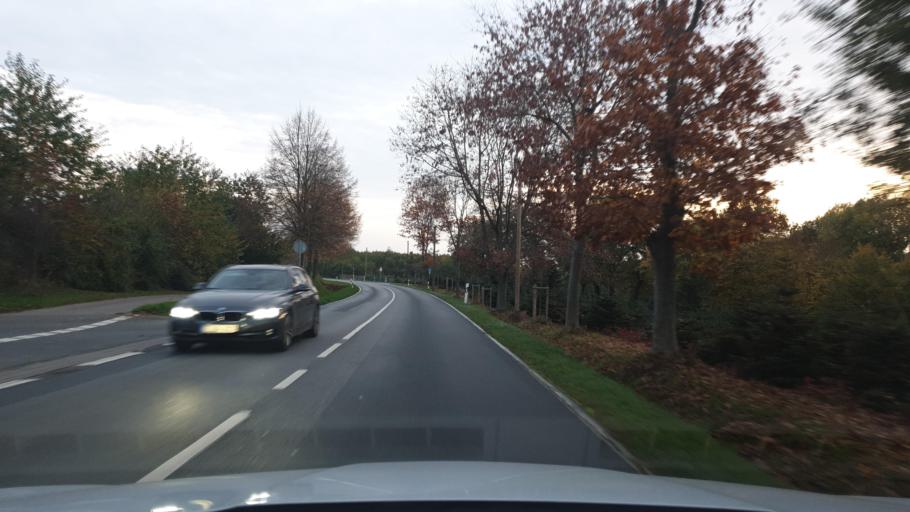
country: DE
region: North Rhine-Westphalia
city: Loehne
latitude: 52.1529
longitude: 8.6800
